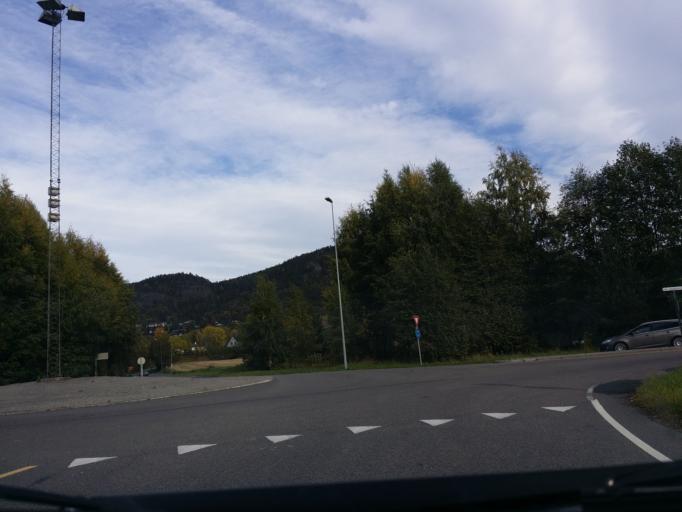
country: NO
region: Akershus
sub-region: Asker
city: Billingstad
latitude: 59.9133
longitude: 10.4916
